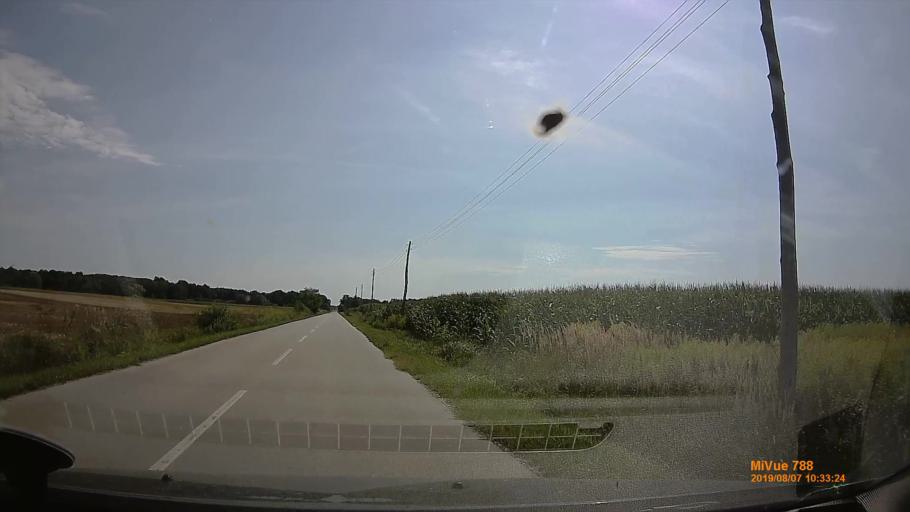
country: SI
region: Lendava-Lendva
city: Lendava
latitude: 46.6168
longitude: 16.4120
